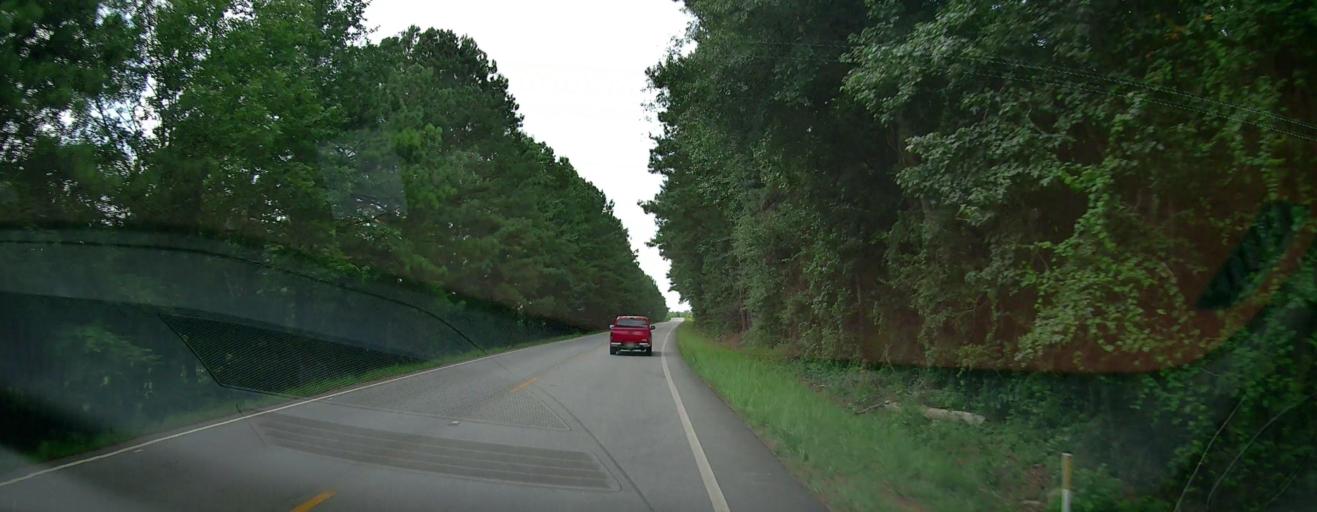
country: US
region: Georgia
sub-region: Meriwether County
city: Greenville
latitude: 33.0703
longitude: -84.7691
